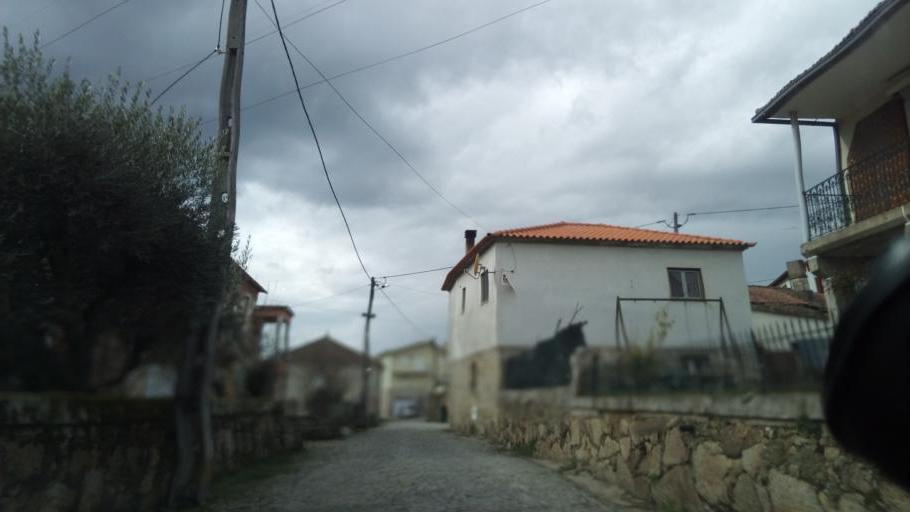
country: PT
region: Guarda
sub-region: Fornos de Algodres
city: Fornos de Algodres
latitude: 40.5874
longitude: -7.4887
